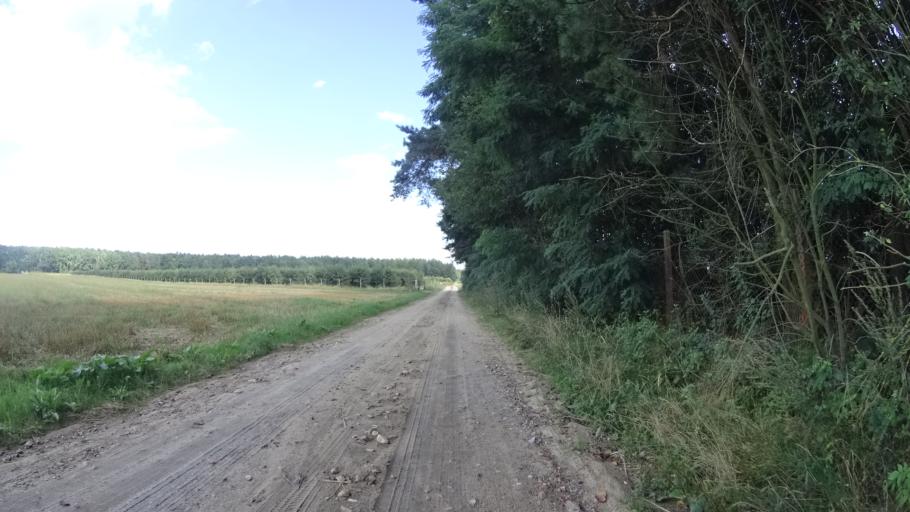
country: PL
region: Masovian Voivodeship
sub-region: Powiat grojecki
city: Mogielnica
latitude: 51.6772
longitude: 20.7740
